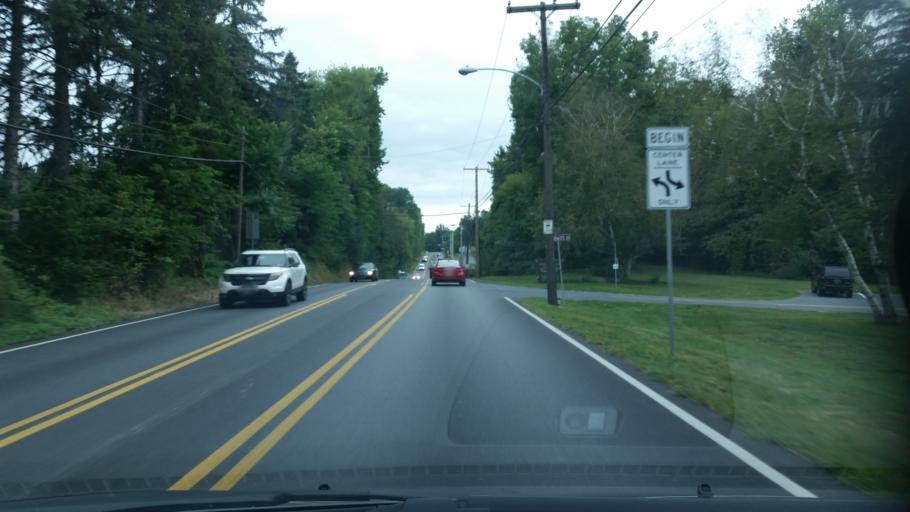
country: US
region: Pennsylvania
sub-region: Lancaster County
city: Lancaster
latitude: 40.0122
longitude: -76.2997
